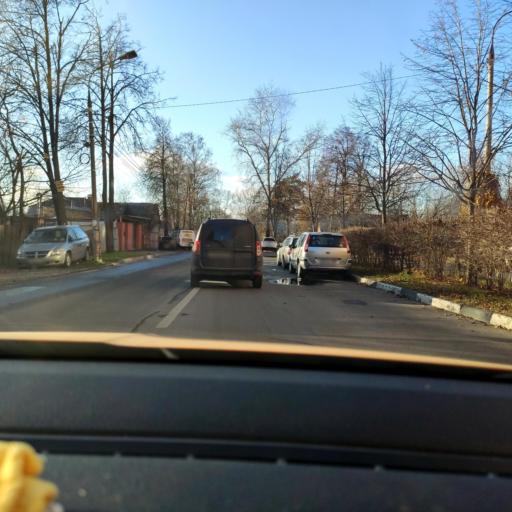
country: RU
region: Moscow
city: Yaroslavskiy
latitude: 55.8956
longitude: 37.7098
